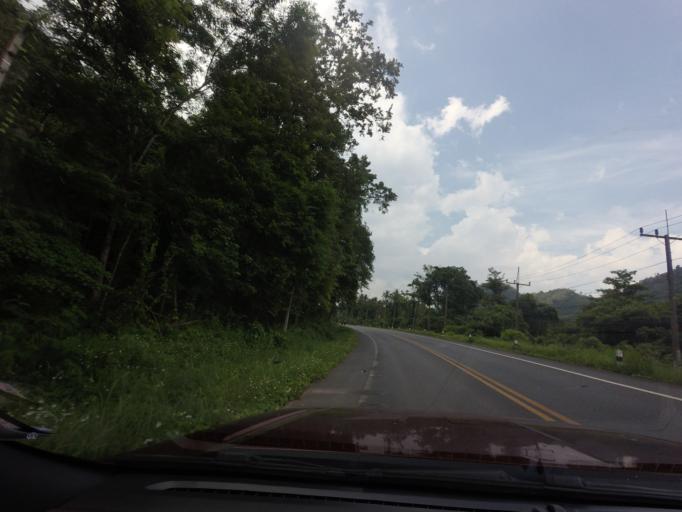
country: TH
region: Yala
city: Ban Nang Sata
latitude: 6.2382
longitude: 101.2179
